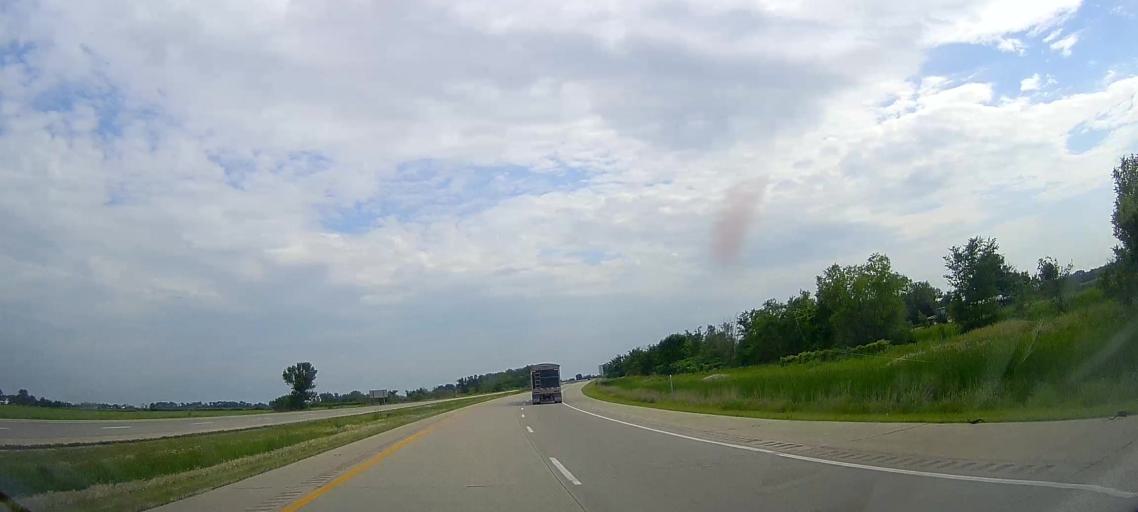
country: US
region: Nebraska
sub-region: Burt County
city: Tekamah
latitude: 41.7947
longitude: -96.0510
